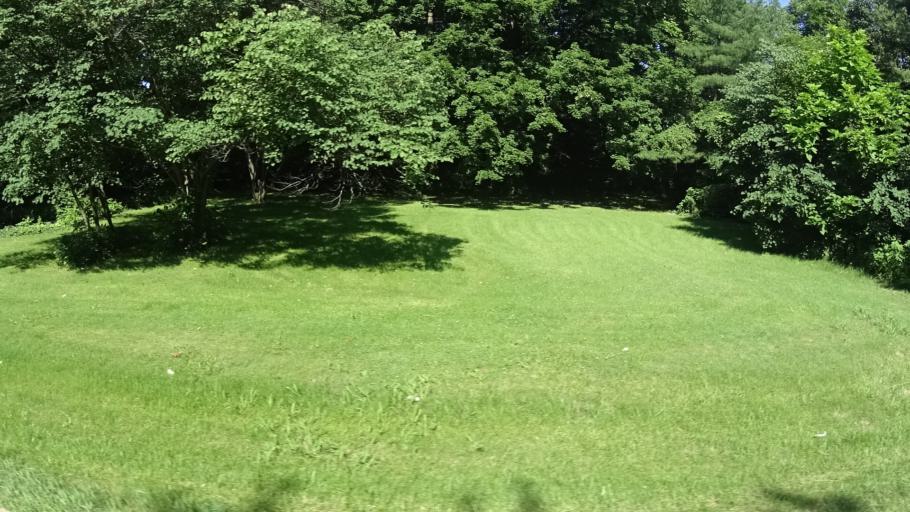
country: US
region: Indiana
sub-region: Hancock County
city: Fortville
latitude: 39.9711
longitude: -85.8433
